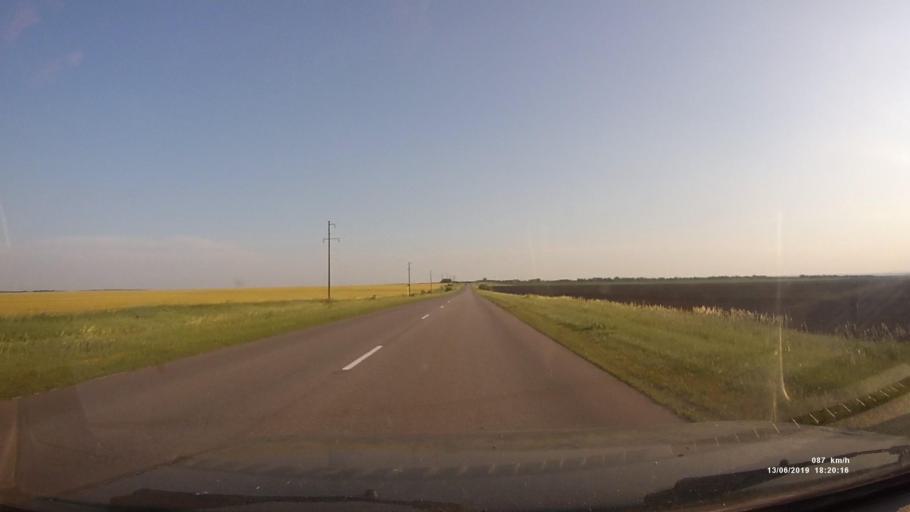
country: RU
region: Rostov
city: Kazanskaya
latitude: 49.8864
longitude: 41.3007
